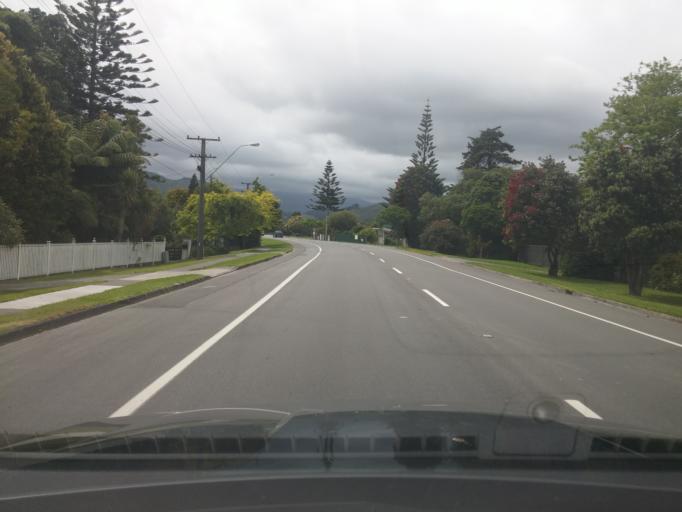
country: NZ
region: Wellington
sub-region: Kapiti Coast District
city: Paraparaumu
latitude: -40.8734
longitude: 175.0386
